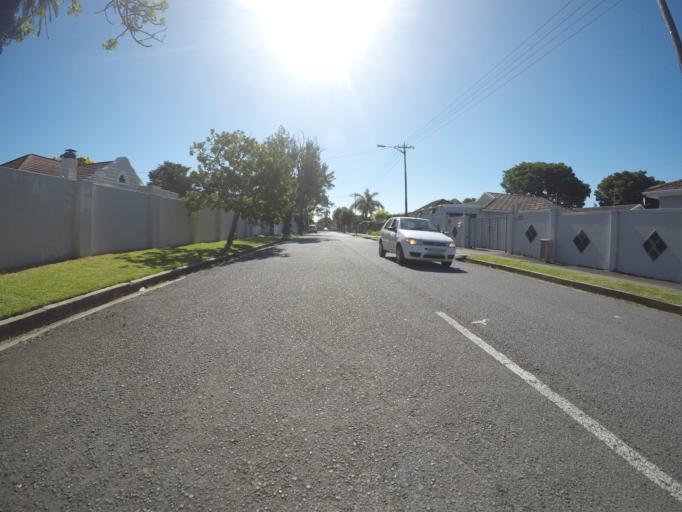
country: ZA
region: Eastern Cape
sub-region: Buffalo City Metropolitan Municipality
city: East London
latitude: -32.9819
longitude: 27.9108
